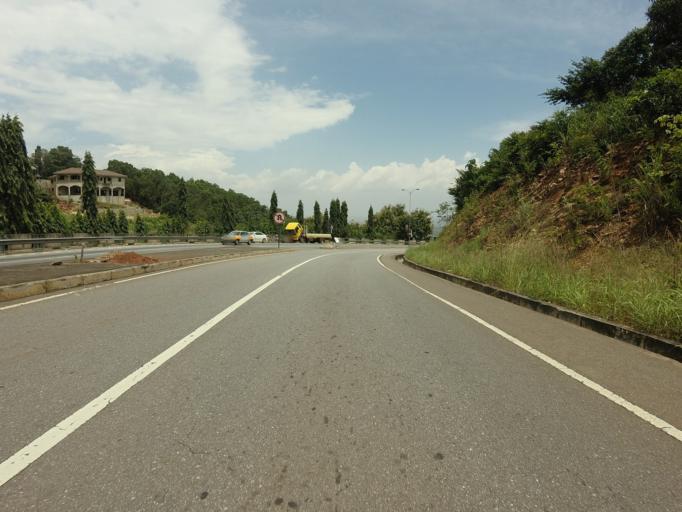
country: GH
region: Eastern
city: Aburi
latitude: 5.7989
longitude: -0.1840
